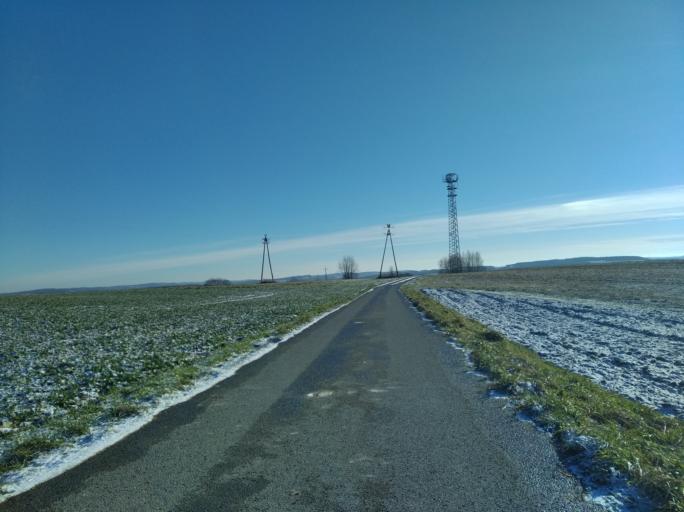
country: PL
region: Subcarpathian Voivodeship
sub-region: Powiat ropczycko-sedziszowski
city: Iwierzyce
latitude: 49.9509
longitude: 21.7611
